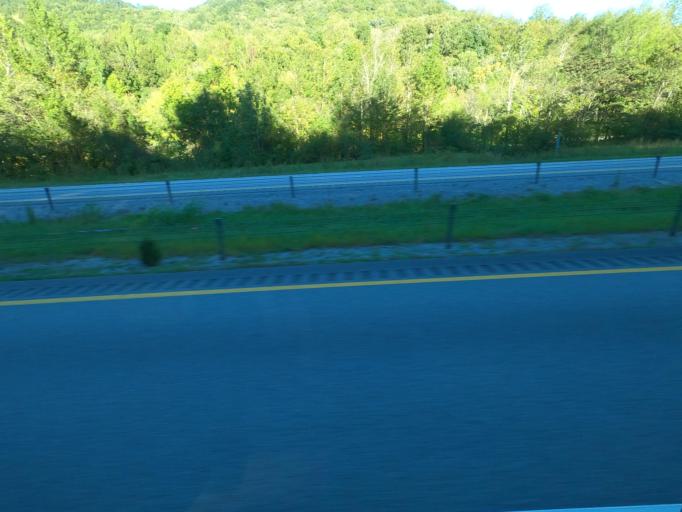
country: US
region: Georgia
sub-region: Dade County
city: Trenton
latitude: 34.9919
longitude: -85.5093
